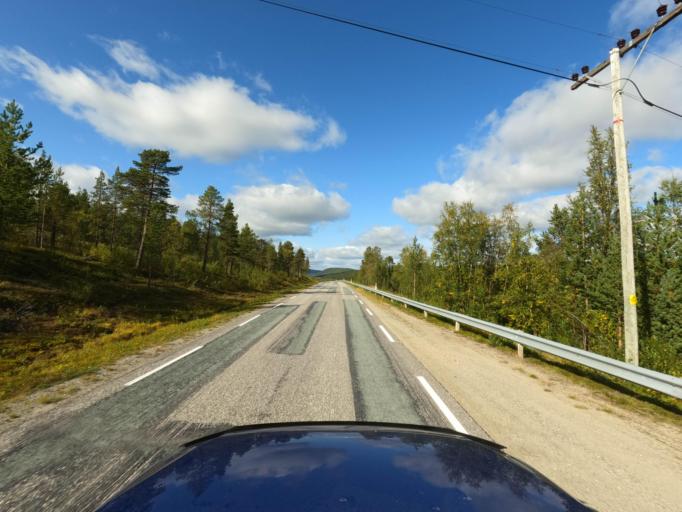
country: NO
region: Finnmark Fylke
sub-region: Karasjok
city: Karasjohka
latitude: 69.4341
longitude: 25.7133
